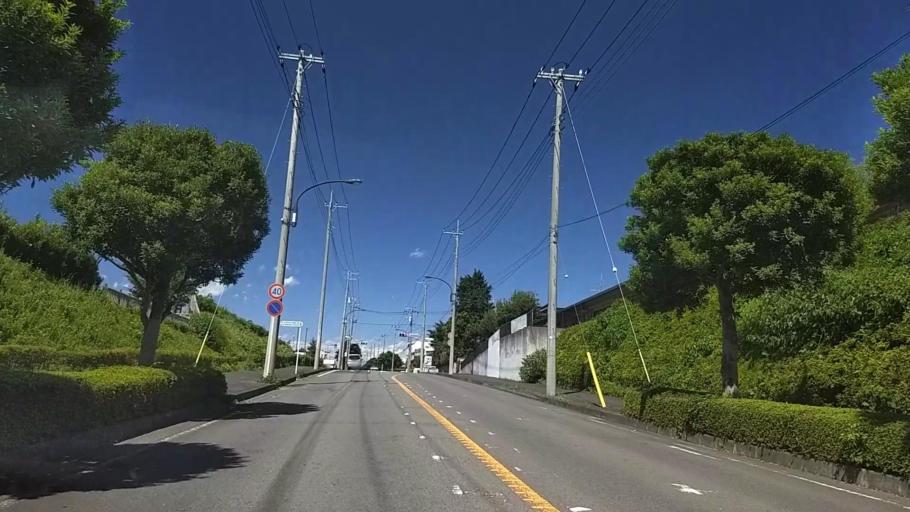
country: JP
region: Kanagawa
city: Zama
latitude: 35.5285
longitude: 139.3561
